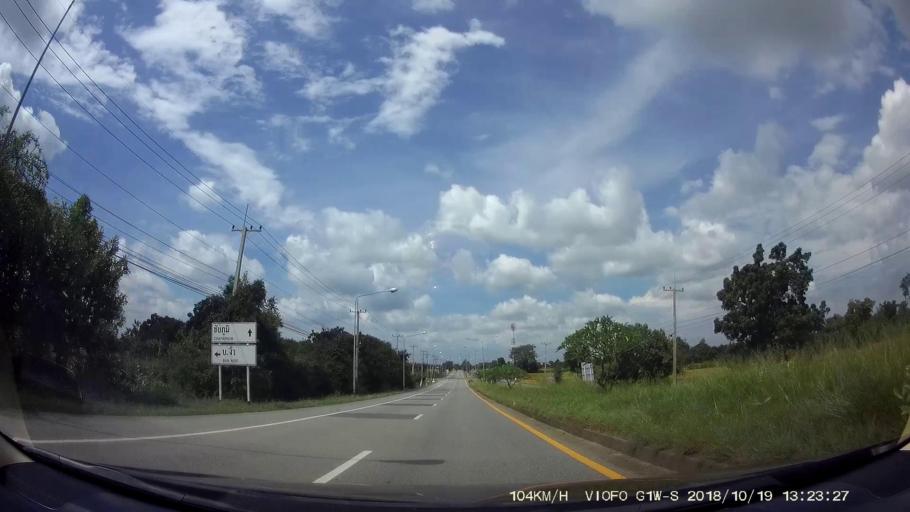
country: TH
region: Chaiyaphum
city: Chatturat
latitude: 15.4922
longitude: 101.8214
